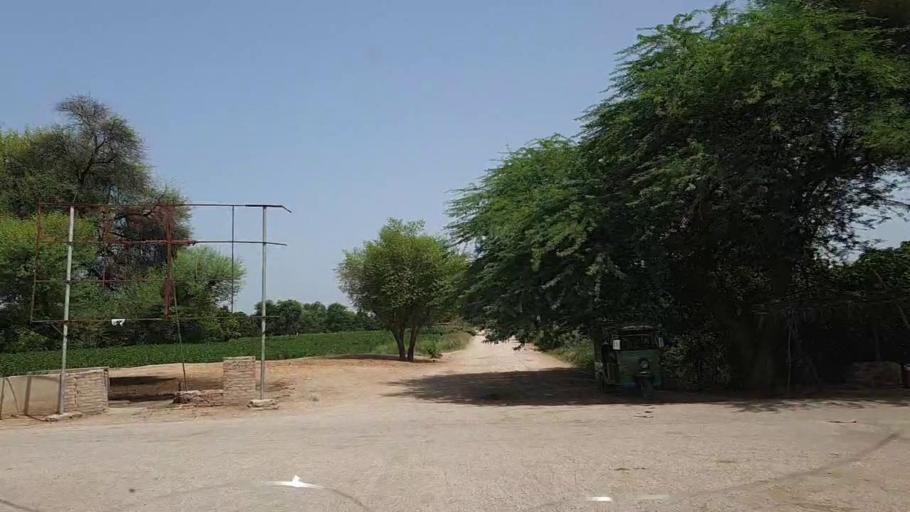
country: PK
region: Sindh
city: Tharu Shah
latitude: 27.0153
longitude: 68.1325
